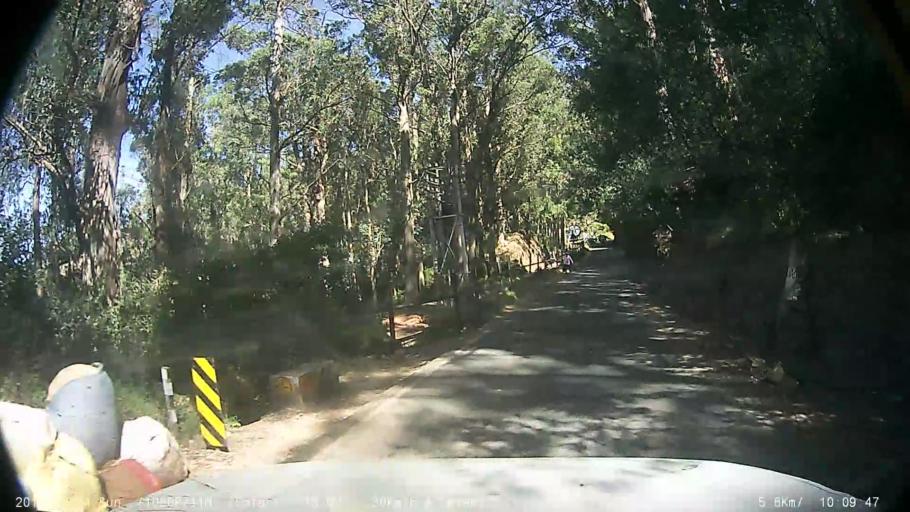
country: IN
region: Tamil Nadu
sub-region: Nilgiri
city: Aravankadu
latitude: 11.3799
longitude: 76.7388
